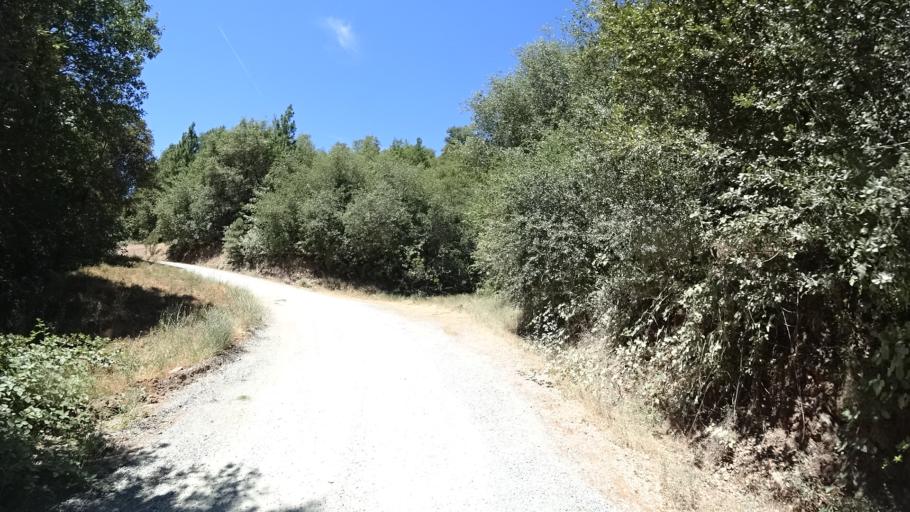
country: US
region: California
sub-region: Calaveras County
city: Murphys
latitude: 38.1523
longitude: -120.4907
